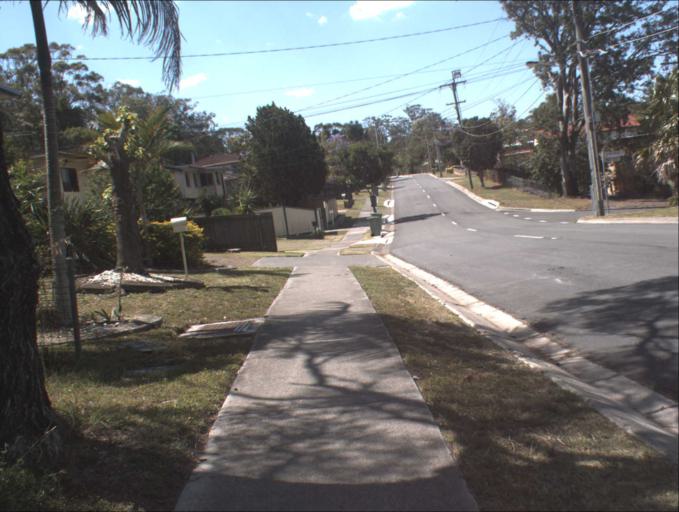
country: AU
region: Queensland
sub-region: Logan
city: Rochedale South
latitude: -27.6014
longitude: 153.1109
